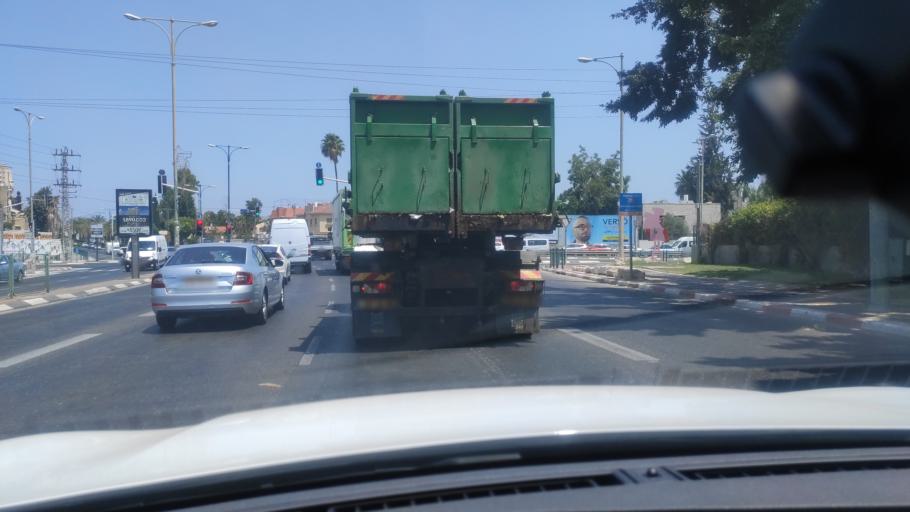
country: IL
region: Central District
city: Petah Tiqwa
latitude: 32.0961
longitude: 34.9017
